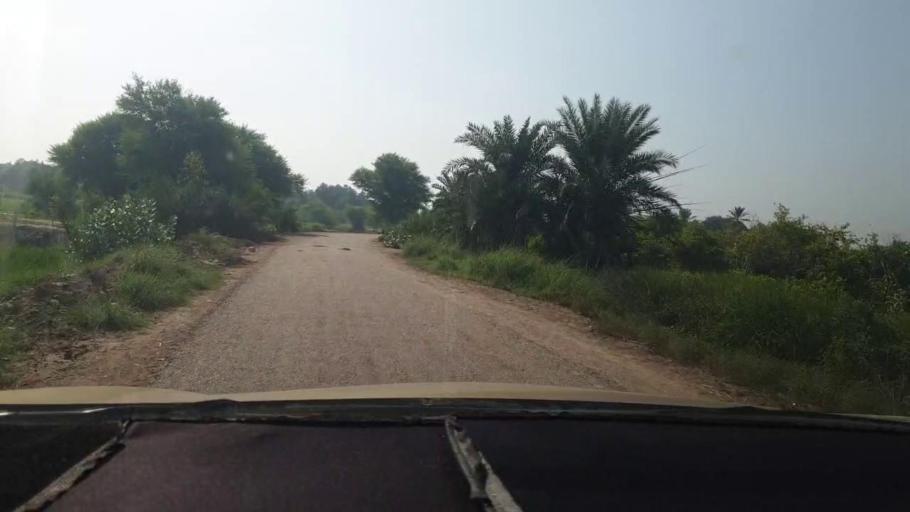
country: PK
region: Sindh
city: Kambar
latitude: 27.6101
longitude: 68.0916
